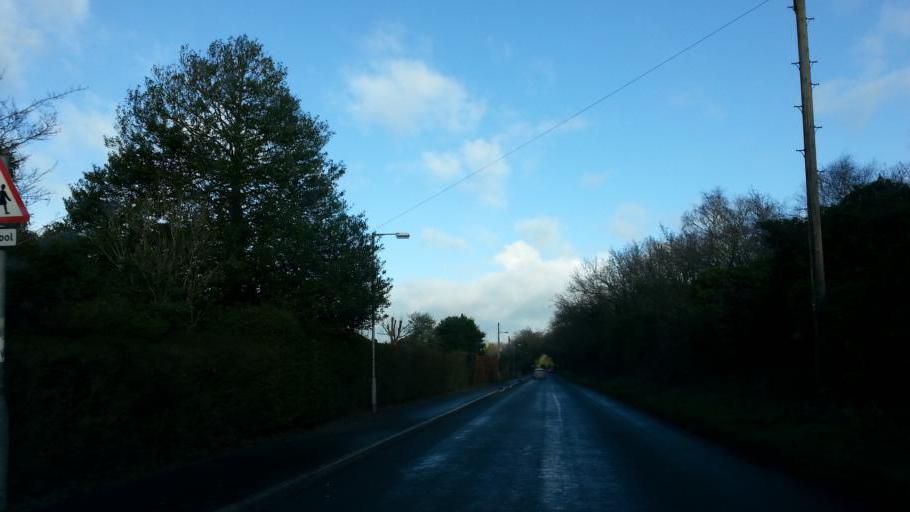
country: GB
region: England
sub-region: Norfolk
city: Ditchingham
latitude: 52.4700
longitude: 1.4488
